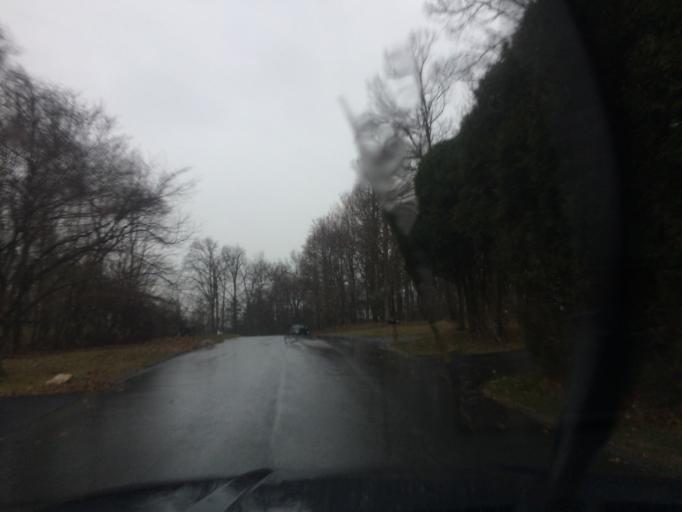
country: US
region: Maryland
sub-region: Carroll County
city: Eldersburg
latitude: 39.3724
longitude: -76.9160
